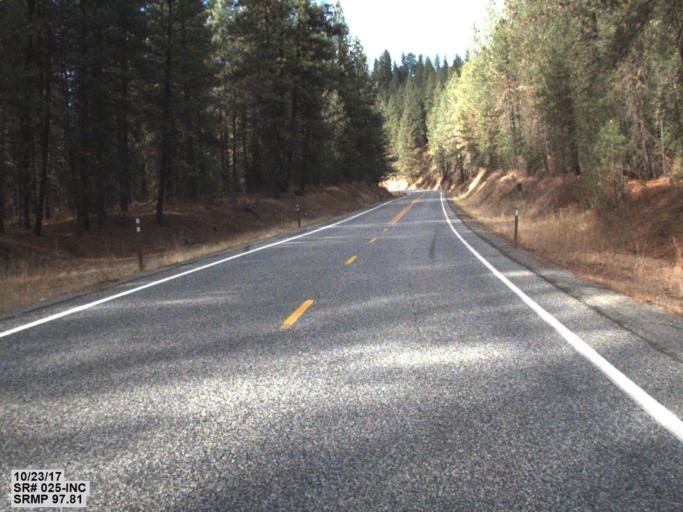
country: US
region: Washington
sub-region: Stevens County
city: Kettle Falls
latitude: 48.7899
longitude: -117.9994
